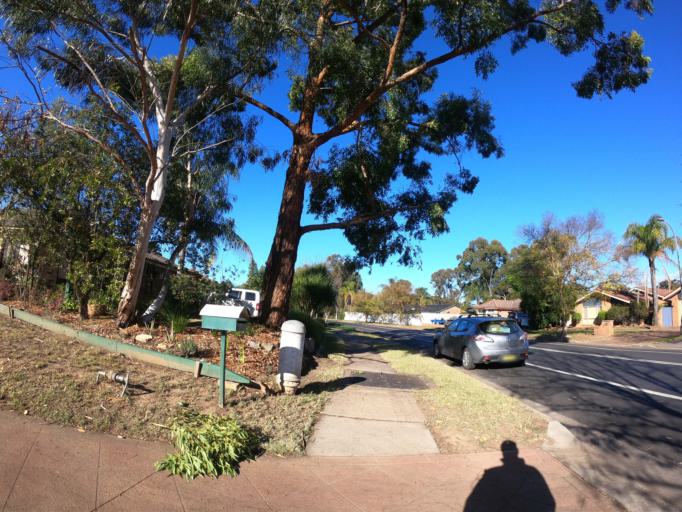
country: AU
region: New South Wales
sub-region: Hawkesbury
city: South Windsor
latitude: -33.6368
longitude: 150.7897
